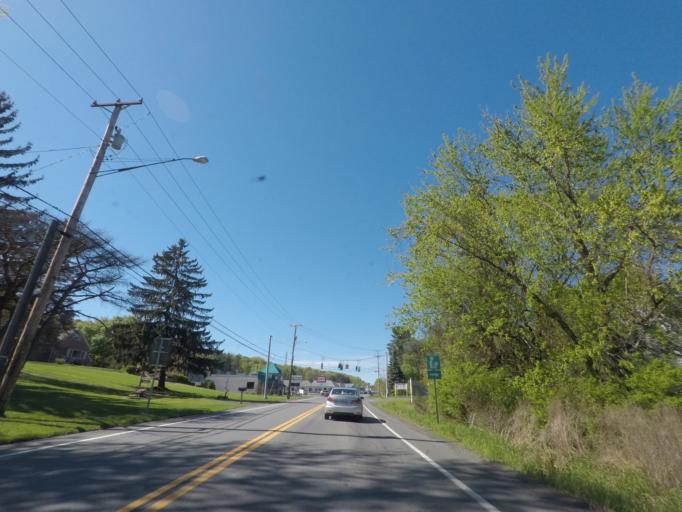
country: US
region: New York
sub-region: Albany County
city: Ravena
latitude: 42.4727
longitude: -73.8180
